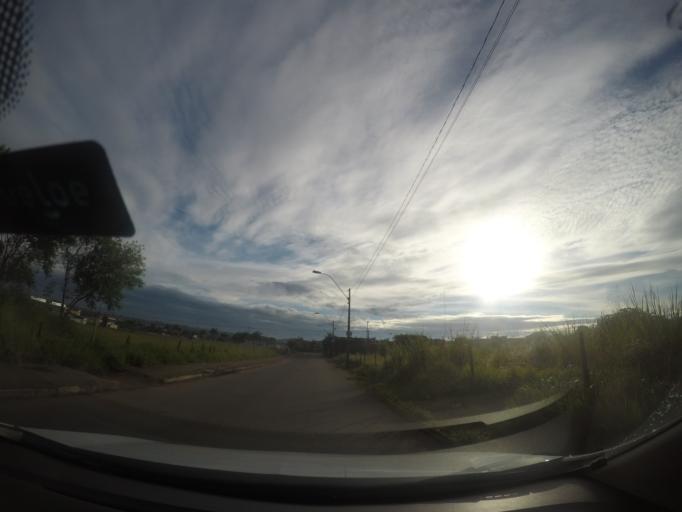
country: BR
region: Goias
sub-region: Goiania
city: Goiania
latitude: -16.6409
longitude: -49.3180
